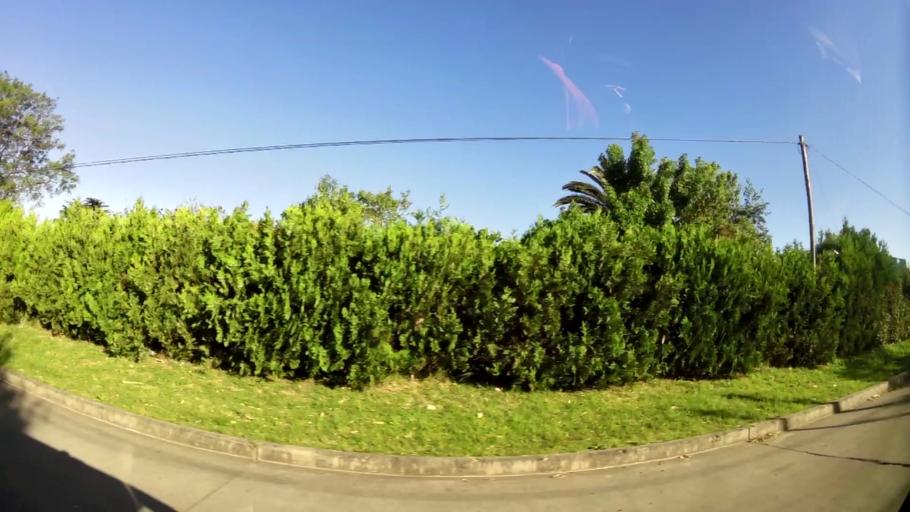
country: UY
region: Canelones
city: La Paz
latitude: -34.8314
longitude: -56.2046
